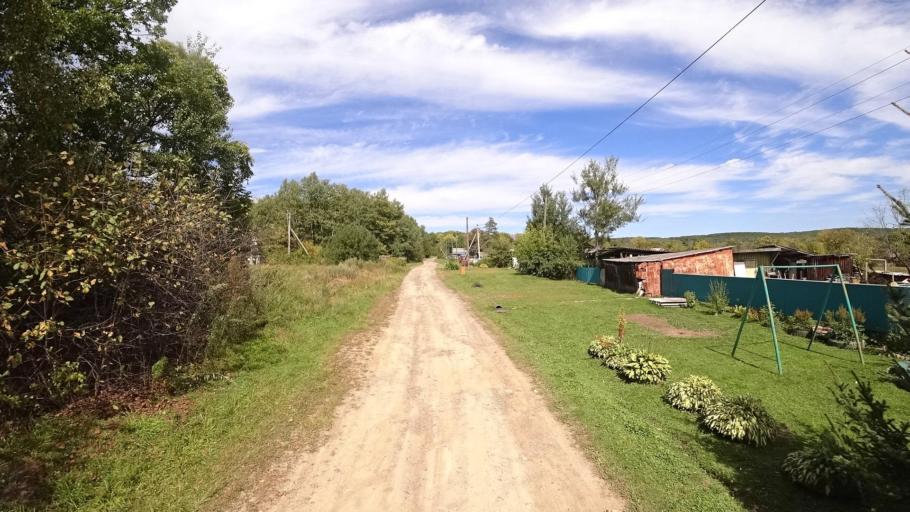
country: RU
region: Primorskiy
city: Yakovlevka
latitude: 44.6475
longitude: 133.5946
